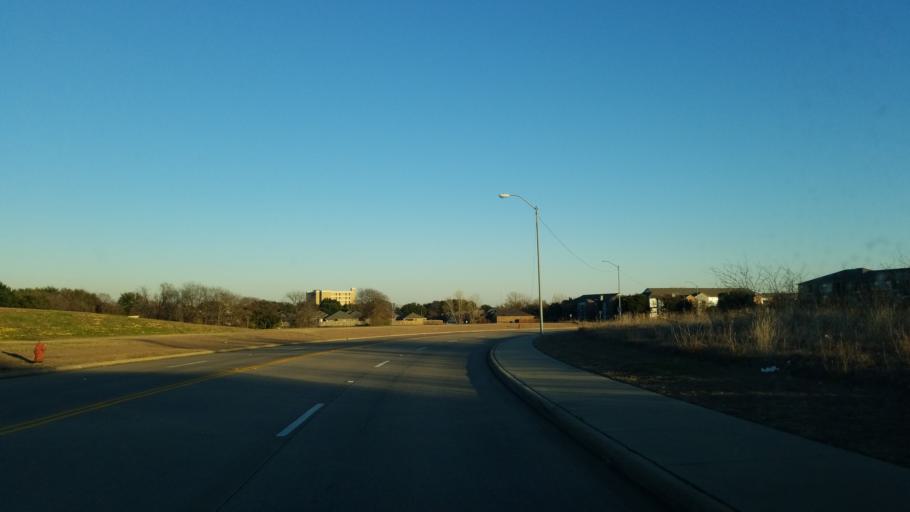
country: US
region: Texas
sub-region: Tarrant County
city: Arlington
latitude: 32.7331
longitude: -97.0564
